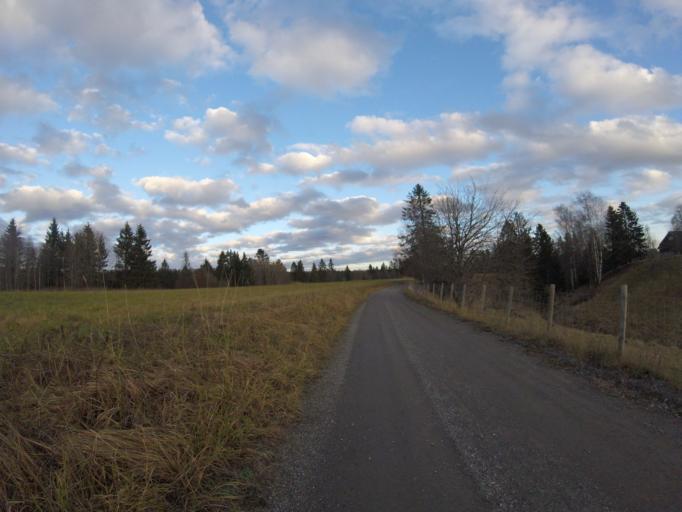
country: NO
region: Akershus
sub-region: Skedsmo
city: Leirsund
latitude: 60.0004
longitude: 11.0523
